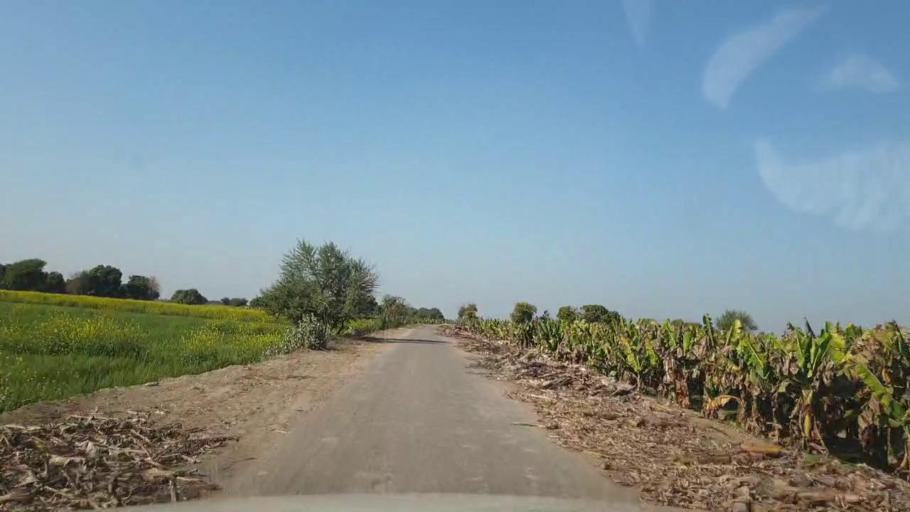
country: PK
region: Sindh
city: Tando Allahyar
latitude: 25.4773
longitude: 68.6603
